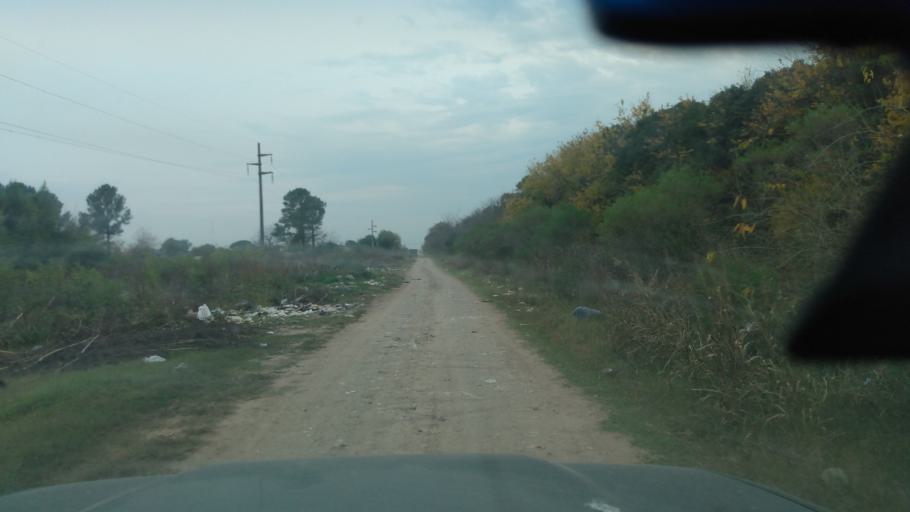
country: AR
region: Buenos Aires
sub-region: Partido de Lujan
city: Lujan
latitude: -34.5581
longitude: -59.1466
